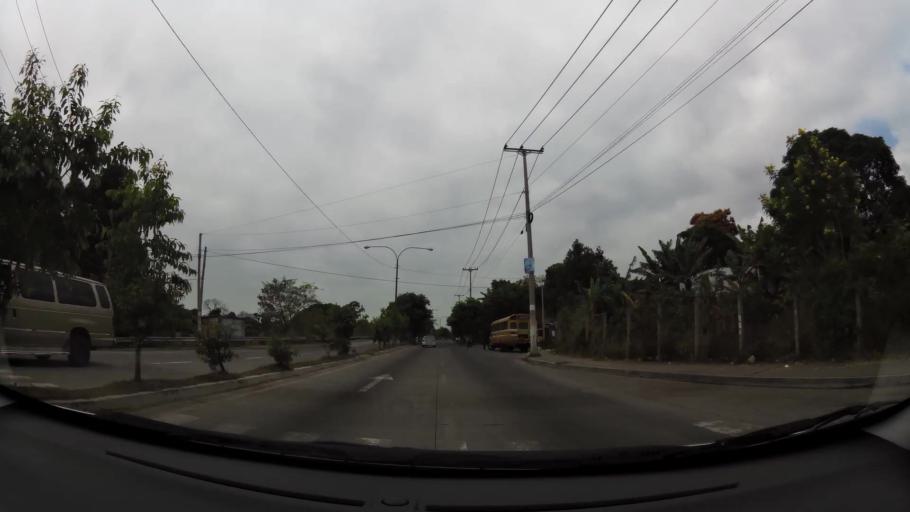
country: SV
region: San Salvador
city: Mejicanos
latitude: 13.7217
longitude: -89.2367
